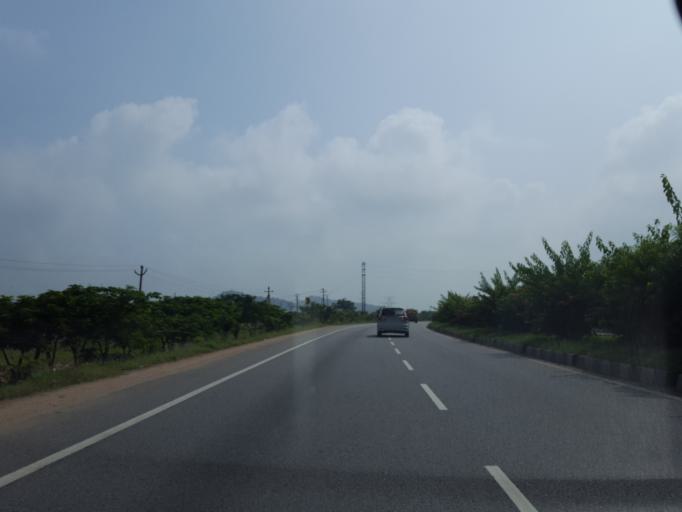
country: IN
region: Telangana
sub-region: Rangareddi
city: Ghatkesar
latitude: 17.2809
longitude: 78.7996
